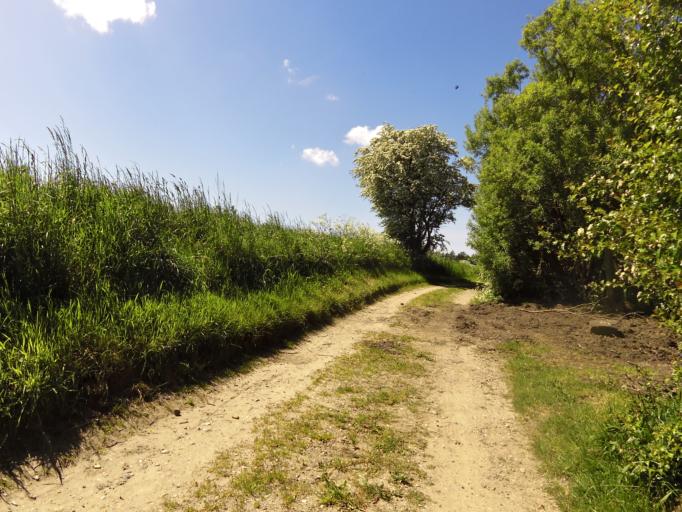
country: DK
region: South Denmark
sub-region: Haderslev Kommune
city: Gram
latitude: 55.2597
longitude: 9.0784
